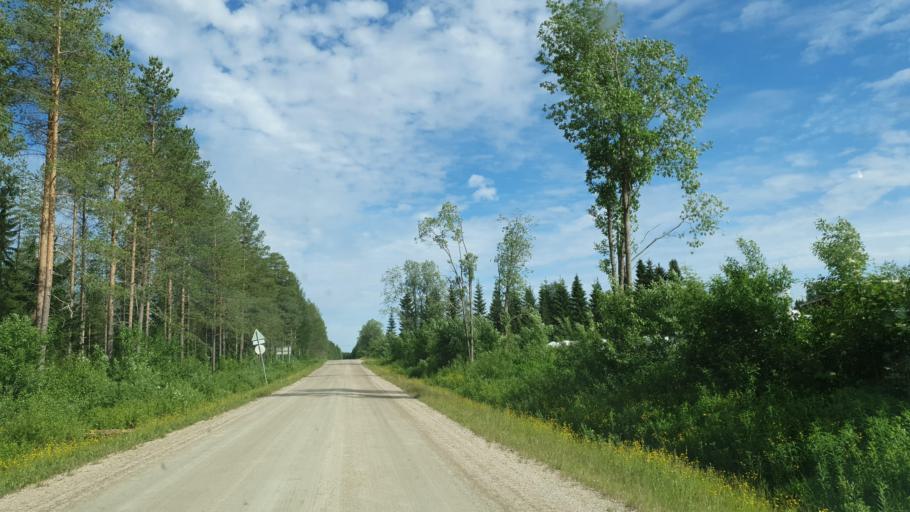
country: FI
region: Kainuu
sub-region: Kehys-Kainuu
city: Kuhmo
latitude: 64.5153
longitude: 29.4045
